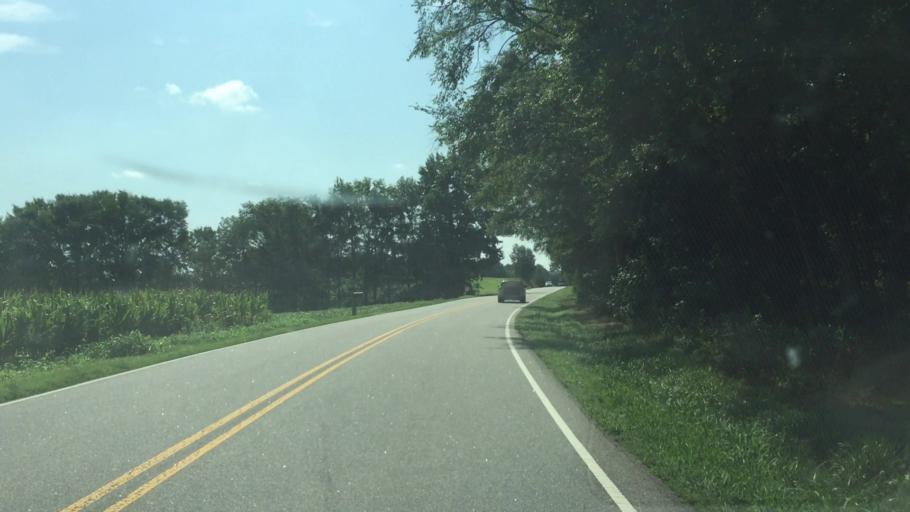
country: US
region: North Carolina
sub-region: Stanly County
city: Oakboro
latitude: 35.1243
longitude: -80.3545
